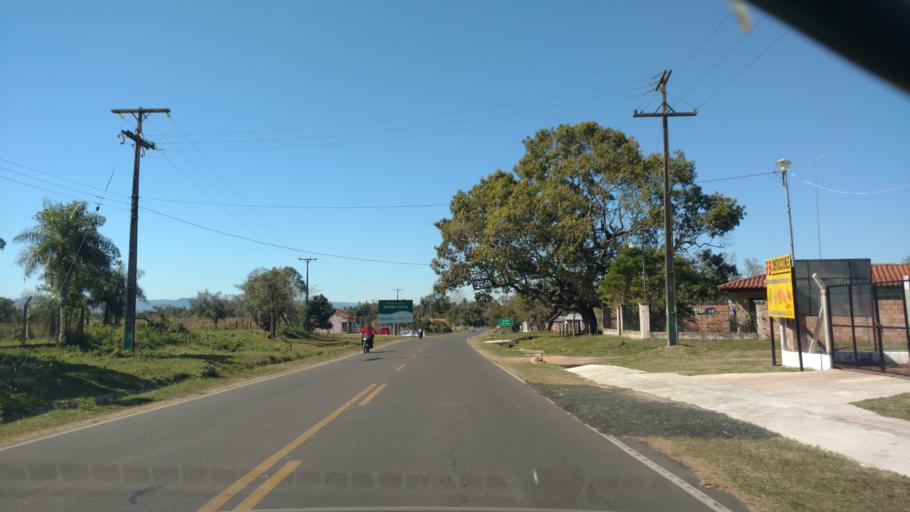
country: PY
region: Central
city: Ypacarai
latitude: -25.4265
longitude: -57.2894
